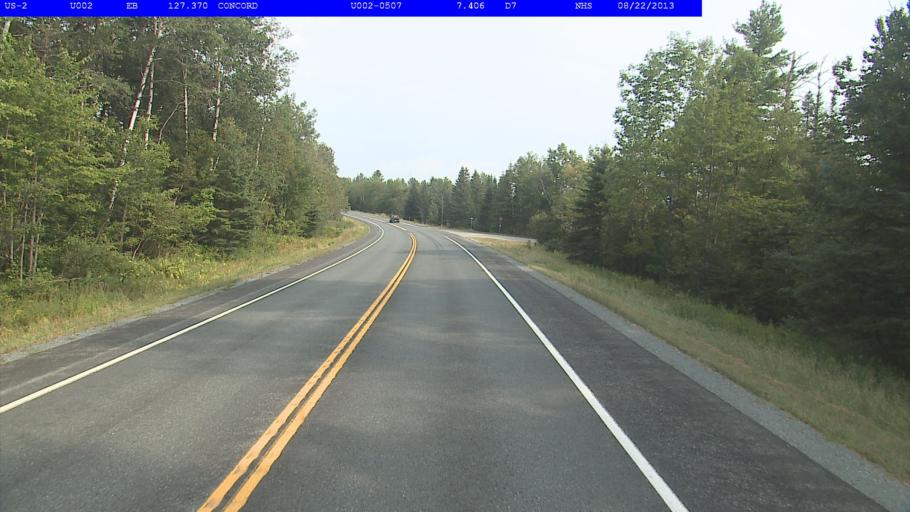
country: US
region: New Hampshire
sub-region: Grafton County
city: Littleton
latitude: 44.4540
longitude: -71.8277
